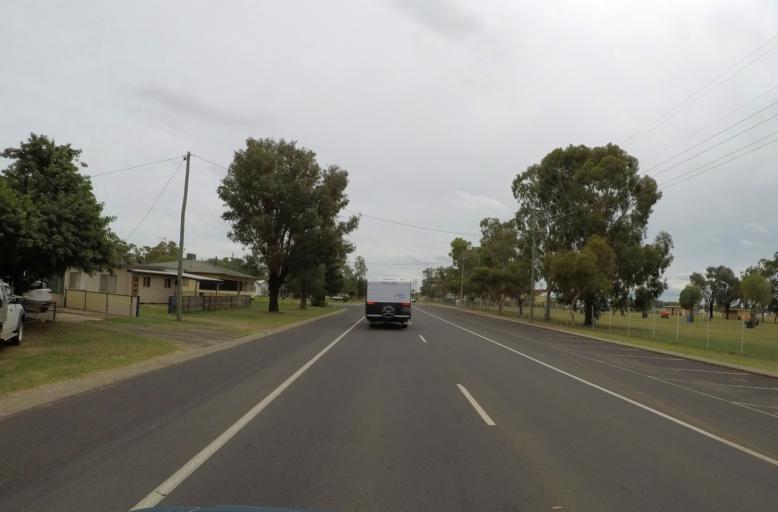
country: AU
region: Queensland
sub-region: Maranoa
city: Roma
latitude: -26.5535
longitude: 148.7848
